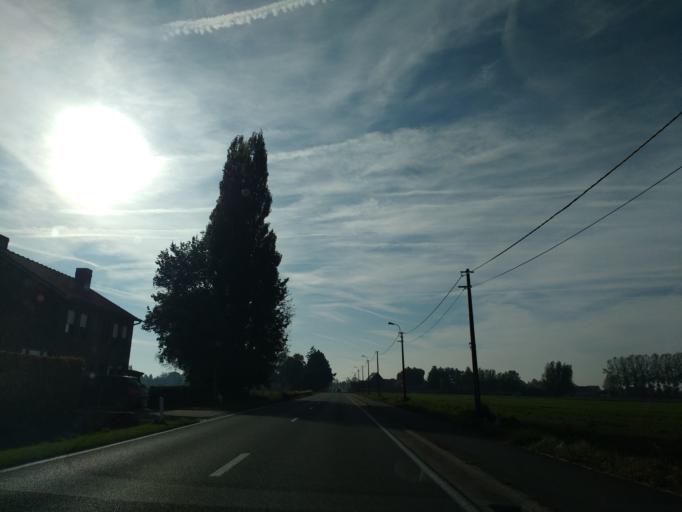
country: BE
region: Flanders
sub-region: Provincie Oost-Vlaanderen
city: Kaprijke
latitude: 51.2549
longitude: 3.6139
